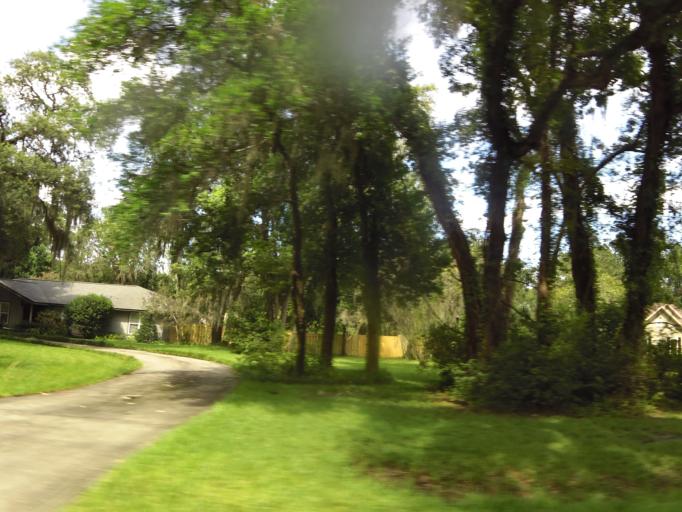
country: US
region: Florida
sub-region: Clay County
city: Lakeside
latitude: 30.1259
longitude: -81.7642
